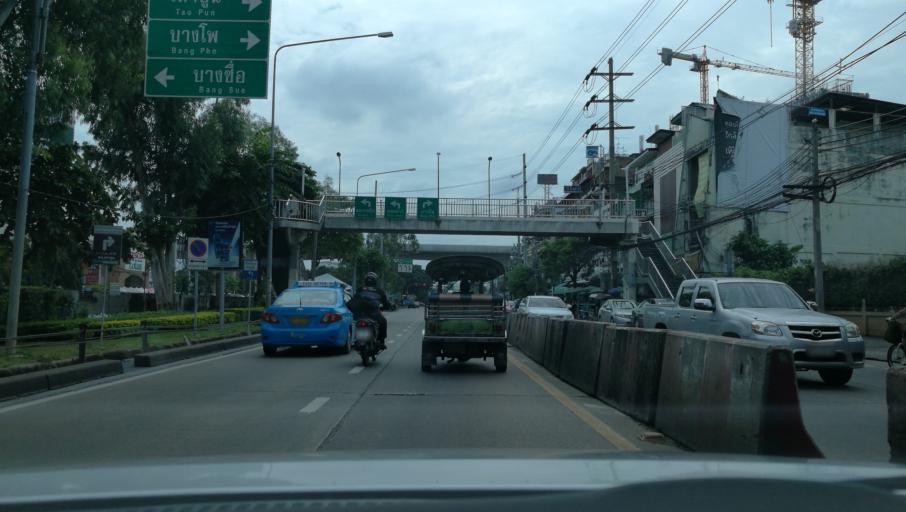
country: TH
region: Bangkok
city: Bang Sue
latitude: 13.8075
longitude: 100.5337
